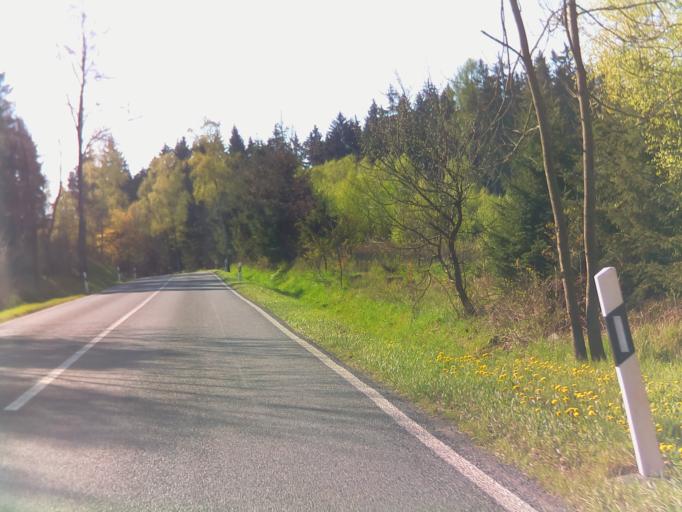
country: DE
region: Thuringia
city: Mossbach
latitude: 50.6685
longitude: 11.7942
